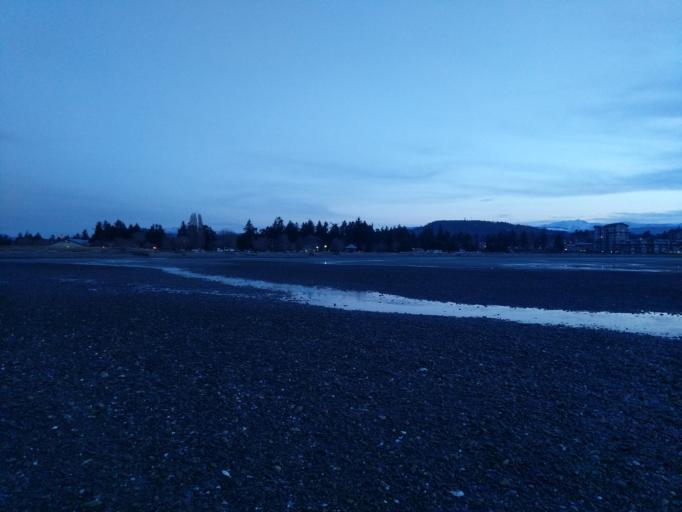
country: CA
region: British Columbia
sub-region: Regional District of Nanaimo
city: Parksville
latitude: 49.3272
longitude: -124.3108
